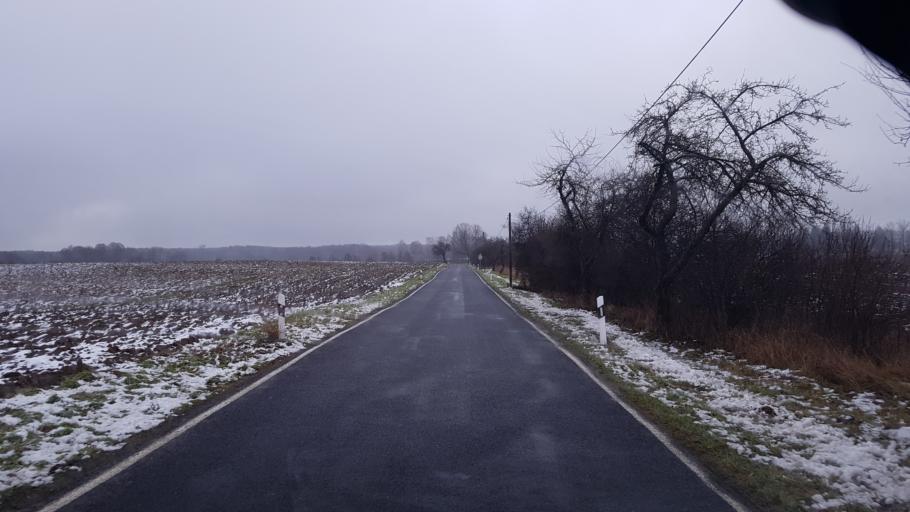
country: DE
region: Brandenburg
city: Lieberose
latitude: 51.9801
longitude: 14.3154
